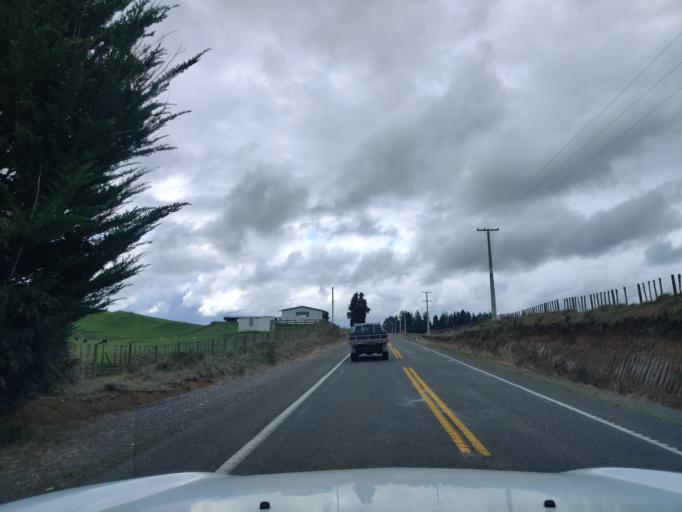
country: NZ
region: Manawatu-Wanganui
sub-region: Ruapehu District
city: Waiouru
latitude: -39.4551
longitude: 175.2932
